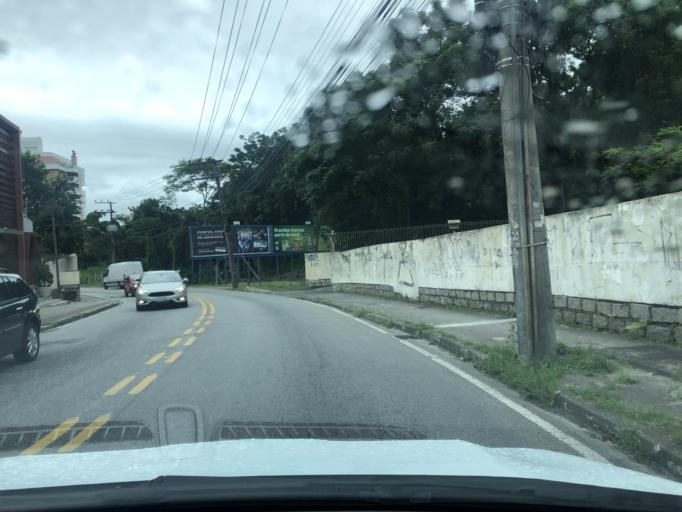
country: BR
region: Santa Catarina
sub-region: Florianopolis
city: Pantanal
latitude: -27.6111
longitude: -48.5248
